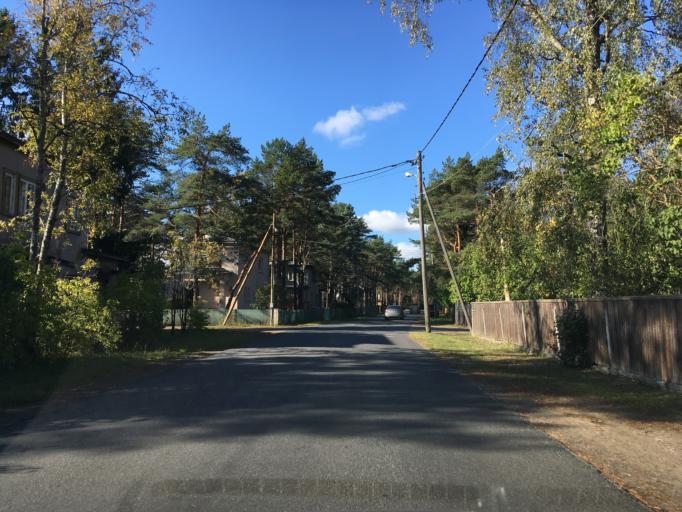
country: EE
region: Harju
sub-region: Saue vald
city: Laagri
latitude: 59.3751
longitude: 24.6876
